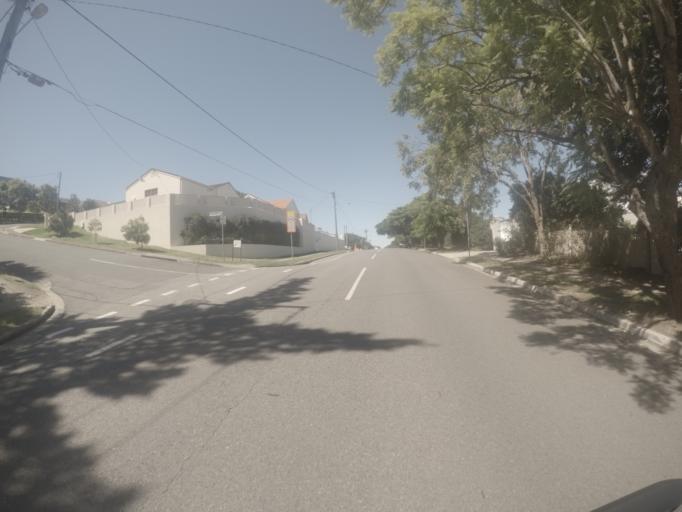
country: AU
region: Queensland
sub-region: Brisbane
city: Ascot
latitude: -27.4272
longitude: 153.0555
